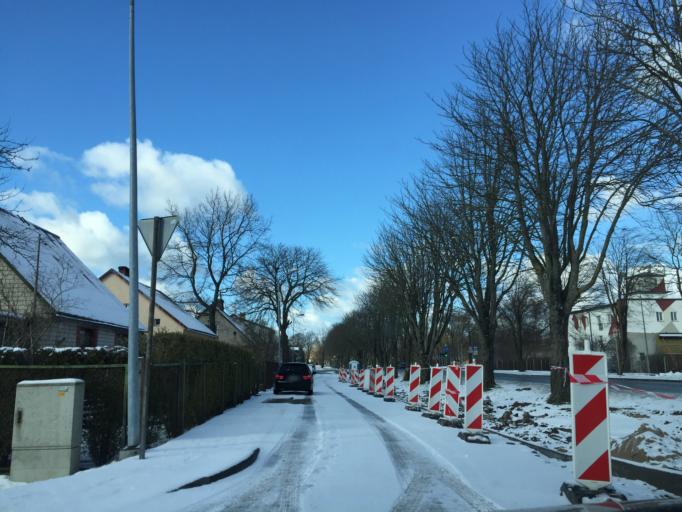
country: LV
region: Ventspils
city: Ventspils
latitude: 57.3808
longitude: 21.5662
